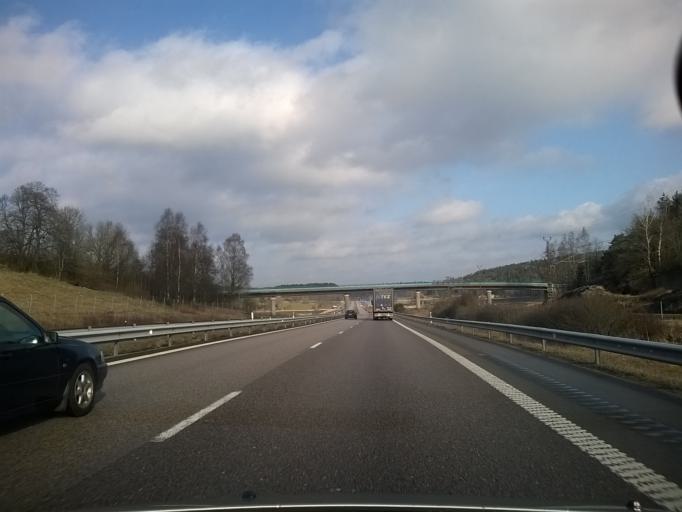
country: SE
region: Vaestra Goetaland
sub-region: Uddevalla Kommun
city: Ljungskile
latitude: 58.2739
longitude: 11.8886
